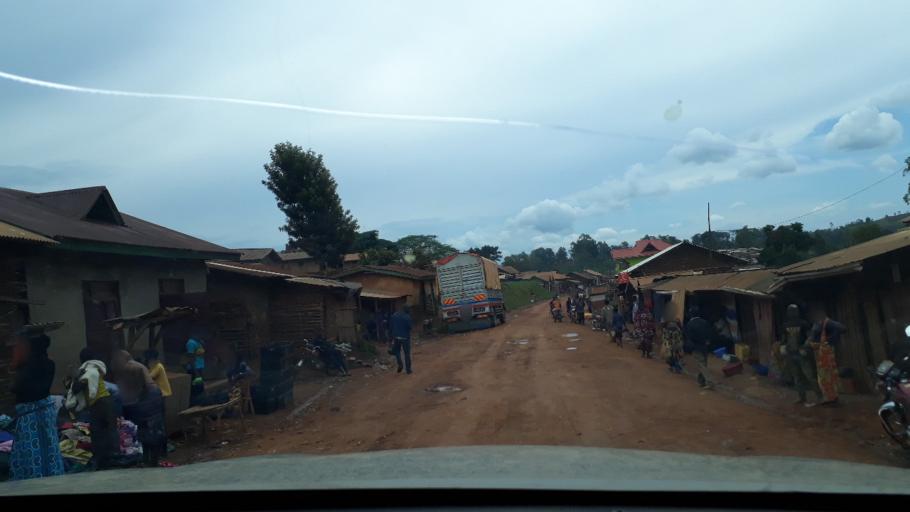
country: CD
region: Eastern Province
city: Bunia
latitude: 1.7381
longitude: 30.3403
